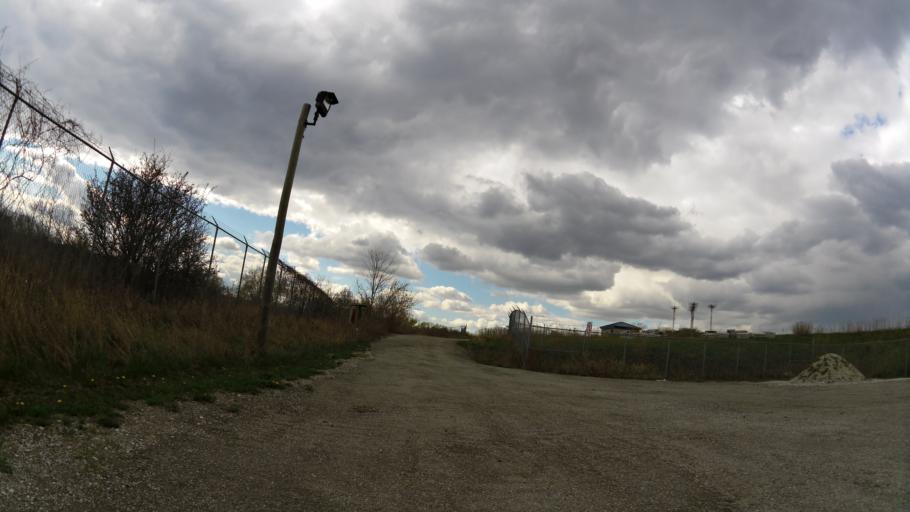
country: CA
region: Ontario
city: Etobicoke
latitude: 43.6617
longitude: -79.6296
